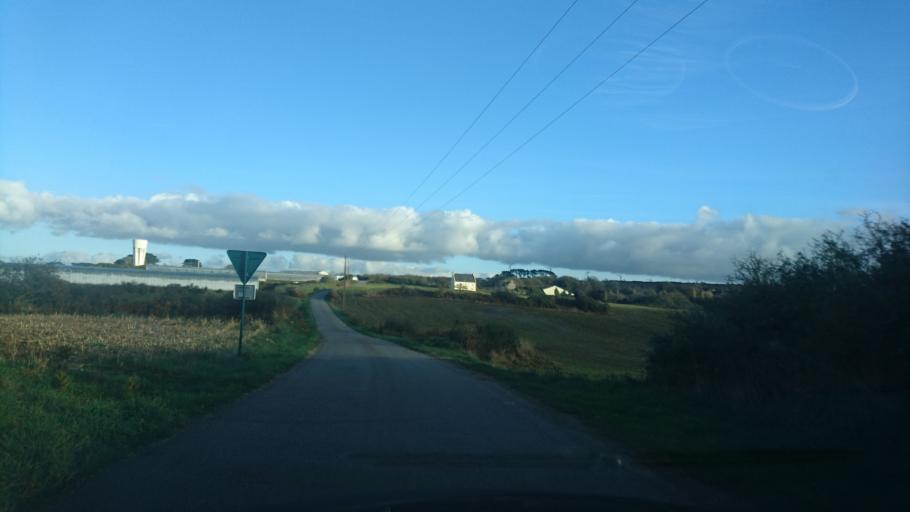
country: FR
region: Brittany
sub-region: Departement du Finistere
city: Lampaul-Plouarzel
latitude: 48.4388
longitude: -4.7659
